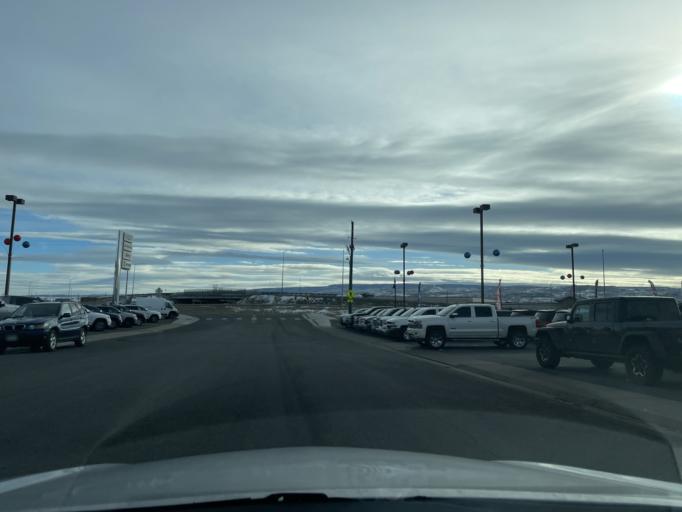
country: US
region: Colorado
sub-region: Mesa County
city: Grand Junction
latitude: 39.0790
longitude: -108.5770
